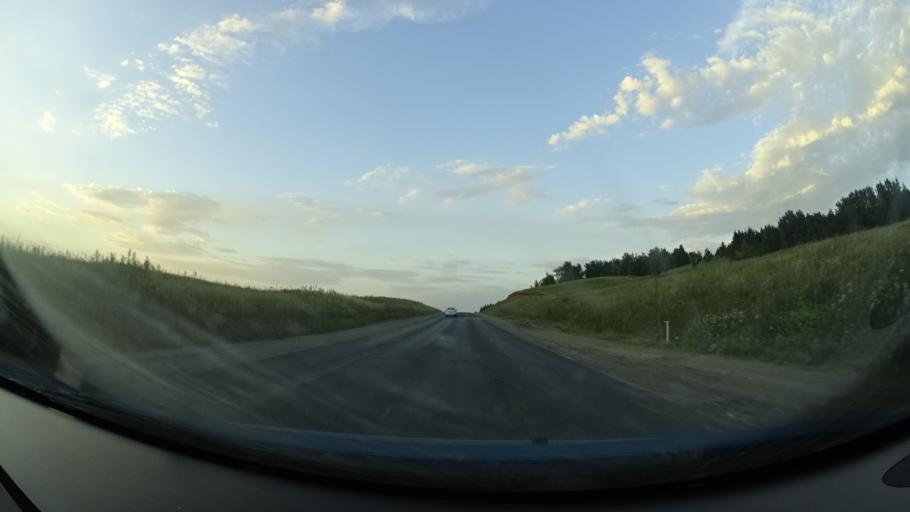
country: RU
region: Orenburg
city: Severnoye
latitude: 54.1705
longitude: 52.6447
